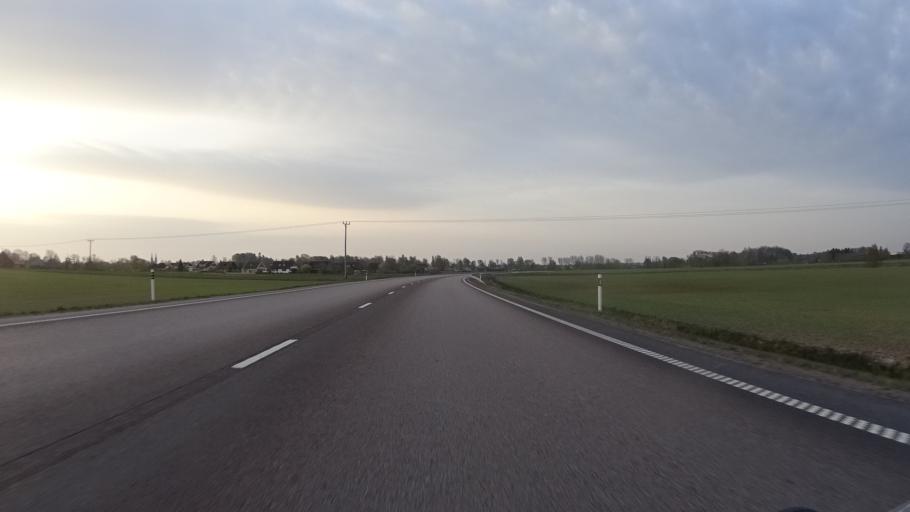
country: SE
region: Vaestra Goetaland
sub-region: Skara Kommun
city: Skara
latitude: 58.3939
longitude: 13.4070
